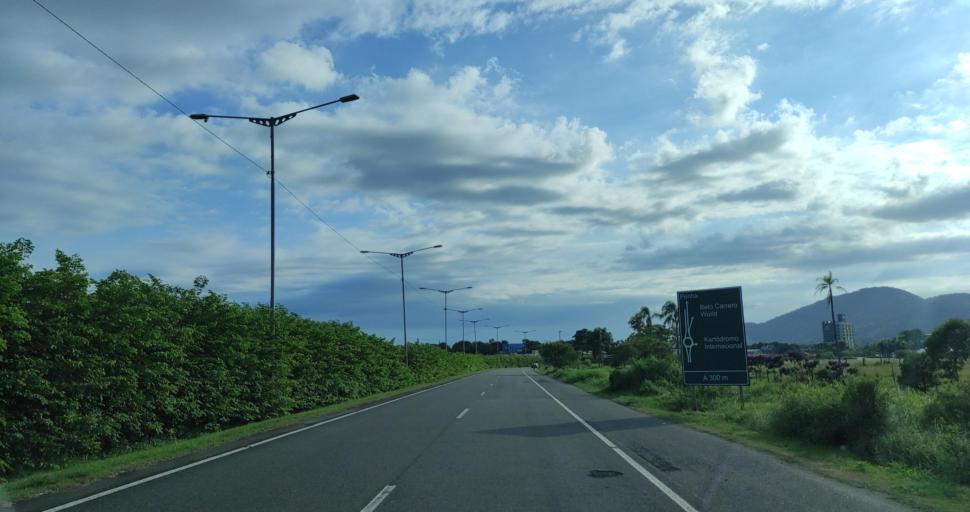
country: BR
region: Santa Catarina
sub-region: Penha
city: Penha
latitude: -26.7990
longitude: -48.6255
